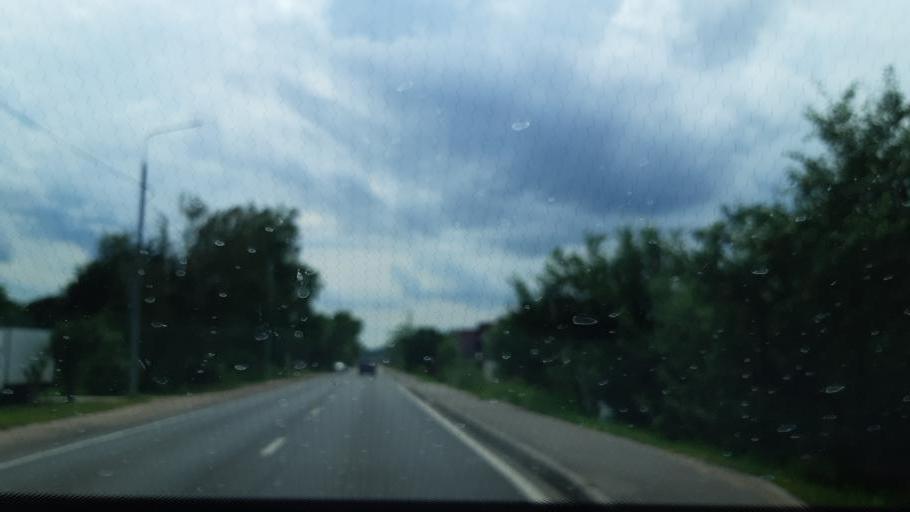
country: RU
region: Moskovskaya
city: Dorokhovo
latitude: 55.5363
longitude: 36.3633
